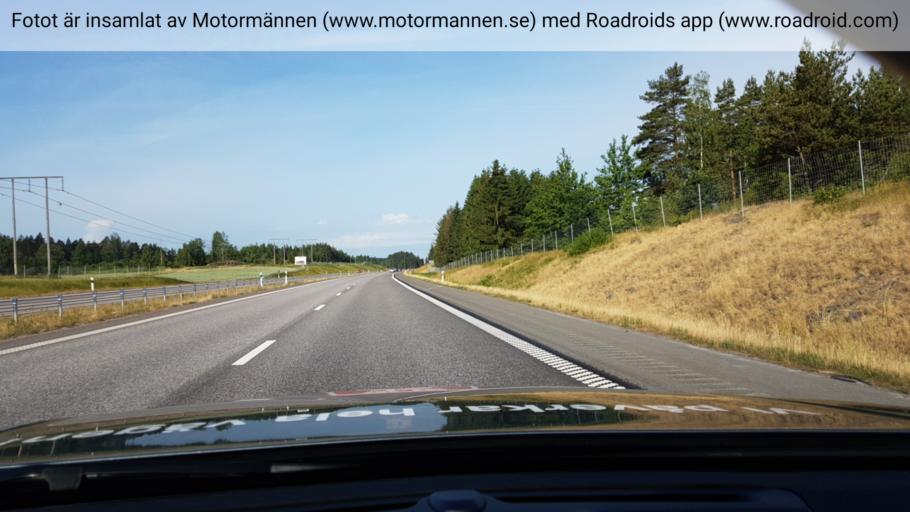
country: SE
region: OEstergoetland
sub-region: Norrkopings Kommun
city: Skarblacka
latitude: 58.4831
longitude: 15.8943
